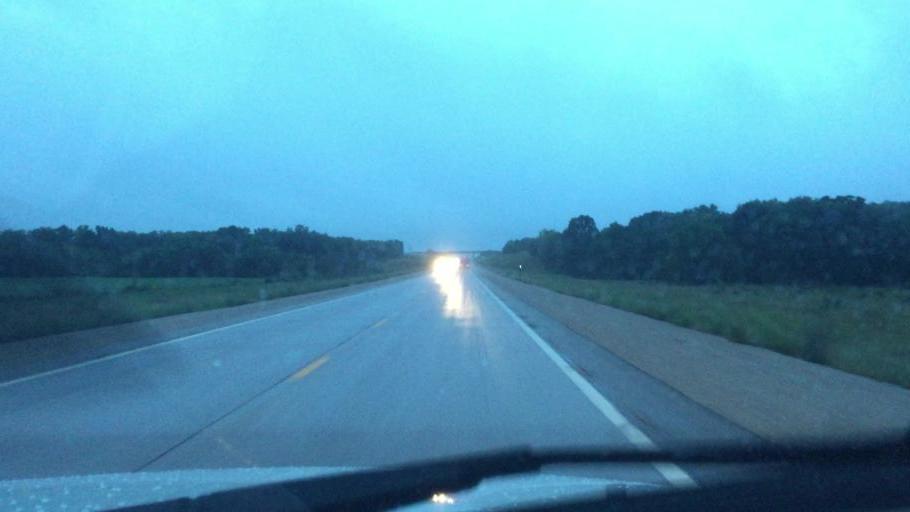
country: US
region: Kansas
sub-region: Allen County
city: Humboldt
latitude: 37.8009
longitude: -95.4114
